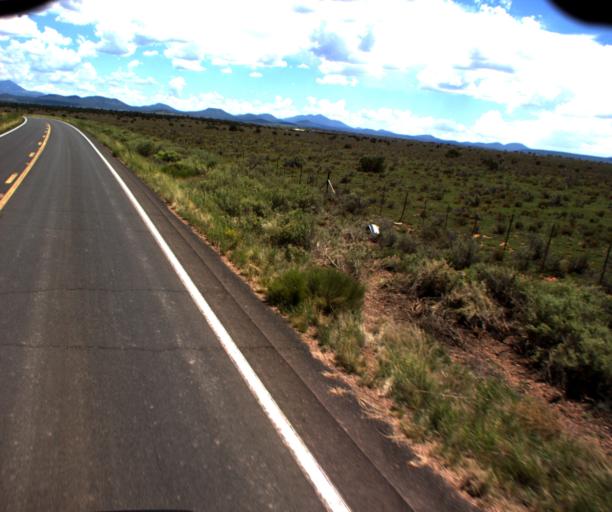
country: US
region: Arizona
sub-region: Coconino County
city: Williams
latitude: 35.6265
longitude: -112.1137
